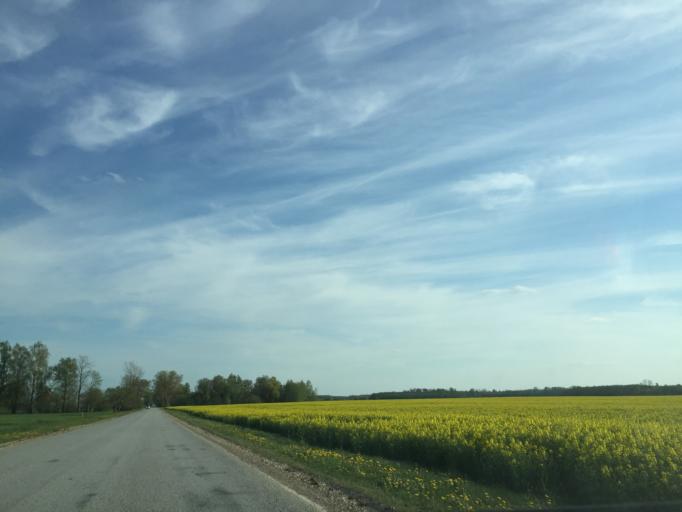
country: LV
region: Bauskas Rajons
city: Bauska
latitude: 56.3609
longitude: 24.2311
